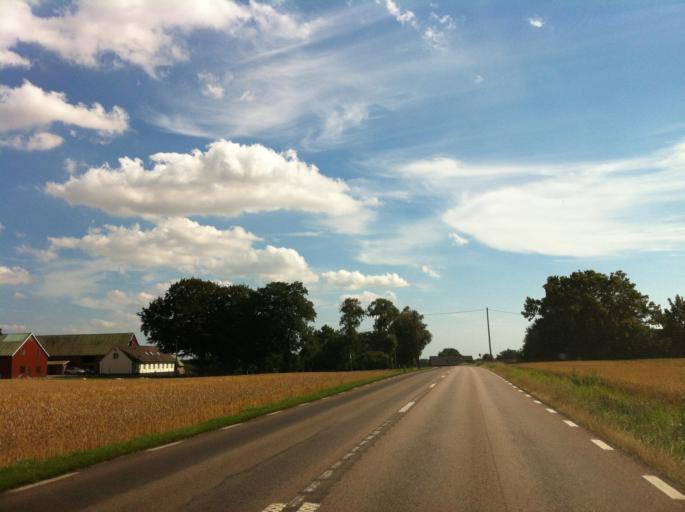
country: SE
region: Skane
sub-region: Helsingborg
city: Glumslov
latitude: 55.9747
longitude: 12.9065
